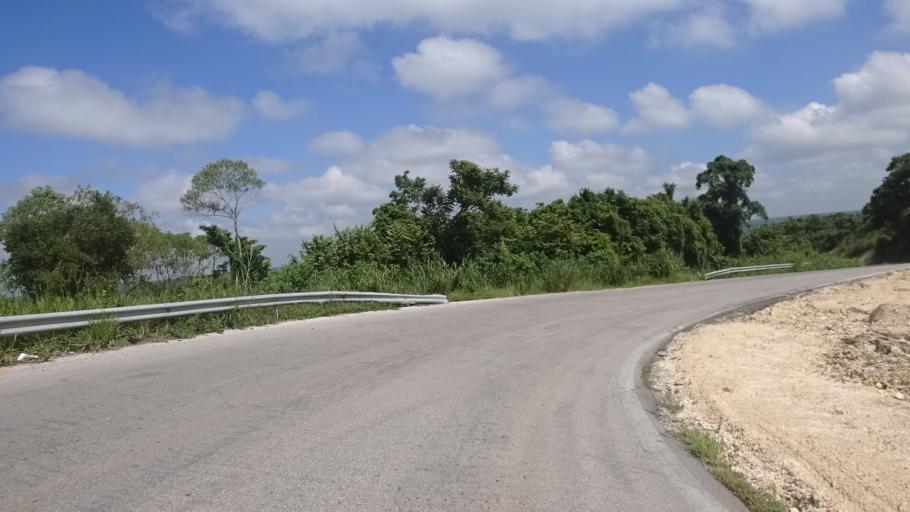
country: MX
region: Chiapas
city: Palenque
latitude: 17.4742
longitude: -91.9670
